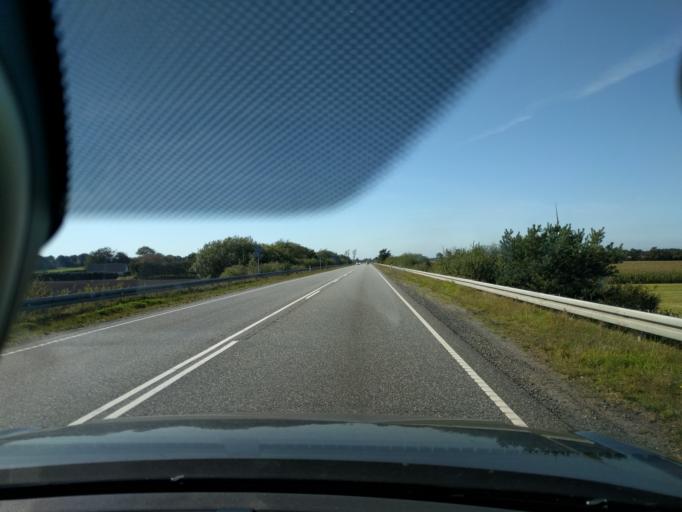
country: DK
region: North Denmark
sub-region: Mariagerfjord Kommune
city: Hobro
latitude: 56.6676
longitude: 9.7316
